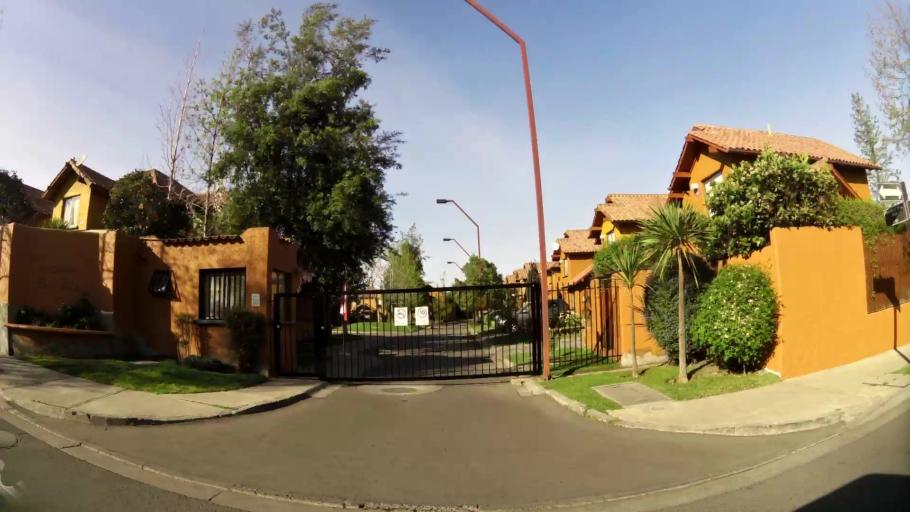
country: CL
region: Santiago Metropolitan
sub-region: Provincia de Santiago
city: Villa Presidente Frei, Nunoa, Santiago, Chile
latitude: -33.4846
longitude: -70.5516
